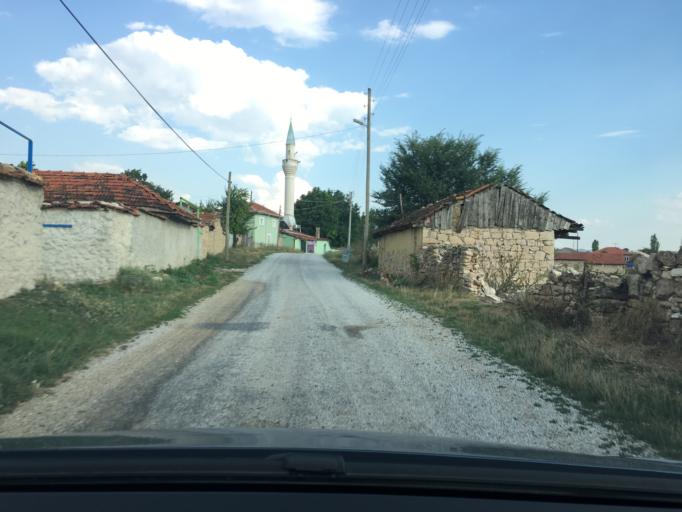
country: TR
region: Eskisehir
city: Kirka
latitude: 39.2771
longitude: 30.6761
